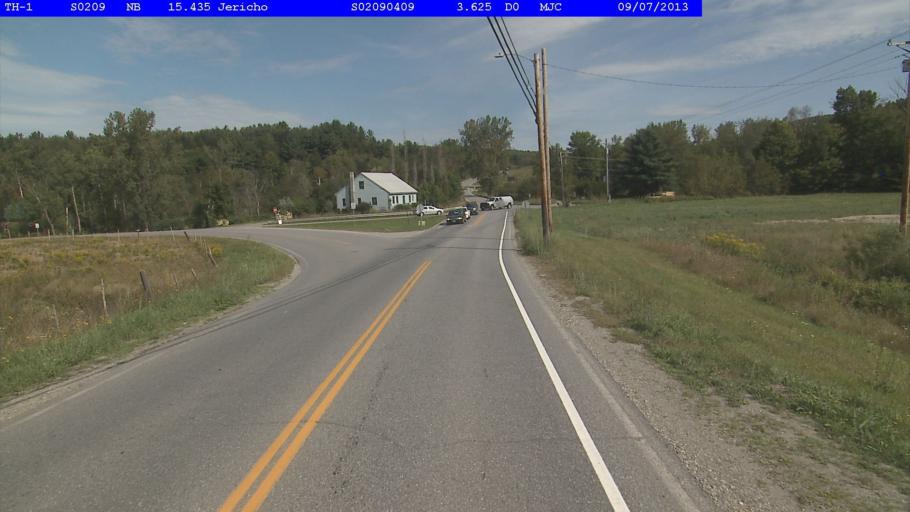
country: US
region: Vermont
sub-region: Chittenden County
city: Jericho
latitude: 44.4798
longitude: -72.9674
